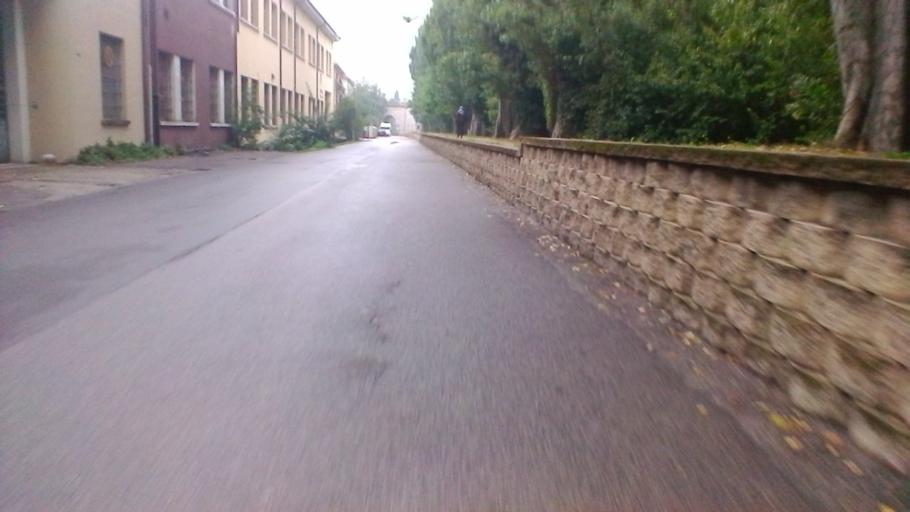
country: IT
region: Veneto
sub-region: Provincia di Verona
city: Verona
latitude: 45.4286
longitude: 10.9973
